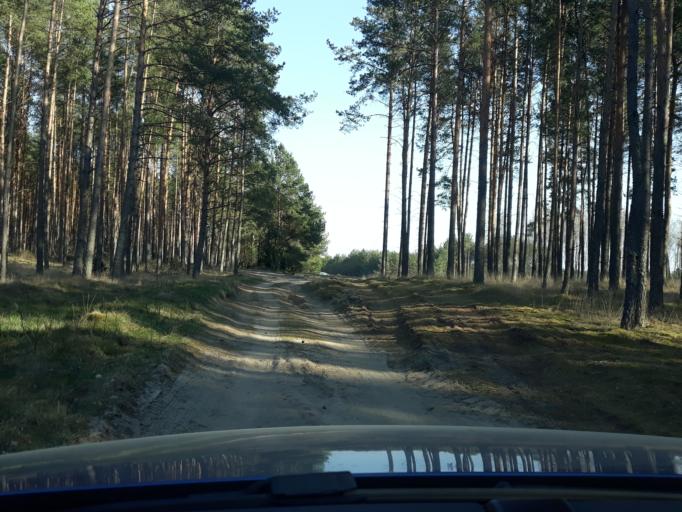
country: PL
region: Pomeranian Voivodeship
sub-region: Powiat bytowski
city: Lipnica
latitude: 53.9201
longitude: 17.4529
